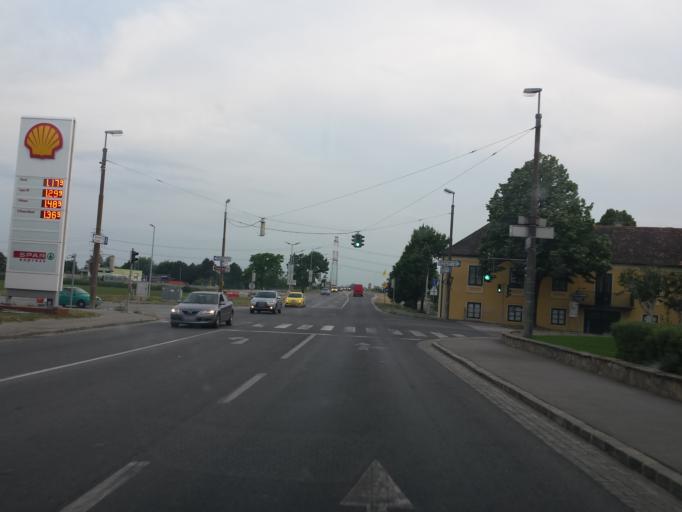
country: AT
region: Lower Austria
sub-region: Politischer Bezirk Ganserndorf
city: Deutsch-Wagram
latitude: 48.2958
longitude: 16.5585
